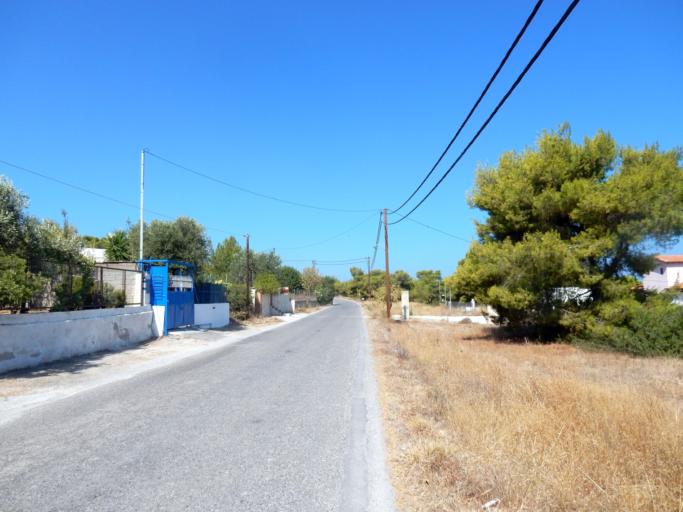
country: GR
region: Attica
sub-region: Nomos Piraios
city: Vathi
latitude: 37.7708
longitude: 23.5220
